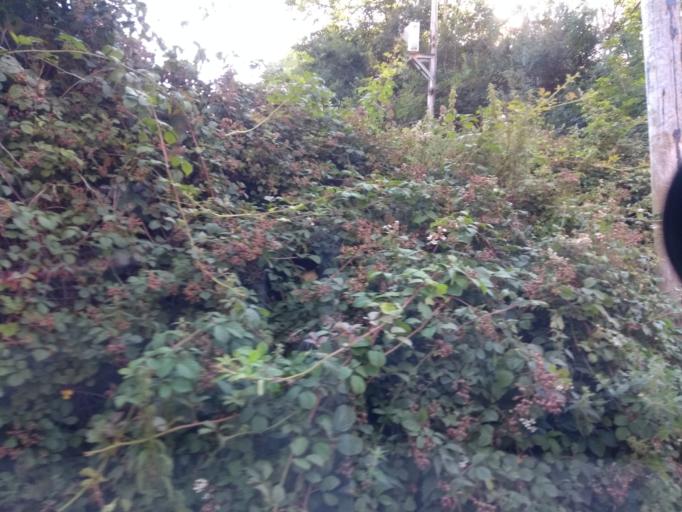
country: GB
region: England
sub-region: Somerset
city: Bishops Lydeard
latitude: 51.1573
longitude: -3.2143
